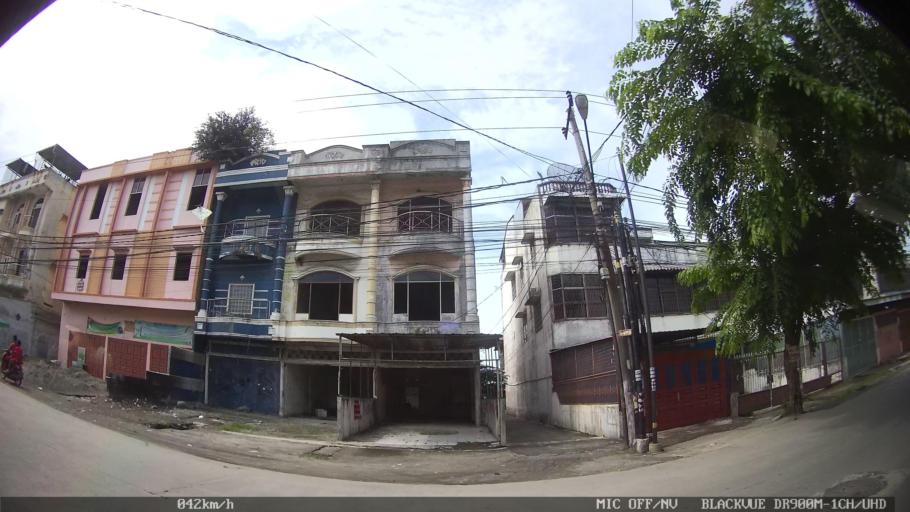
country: ID
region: North Sumatra
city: Medan
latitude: 3.6233
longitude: 98.6736
